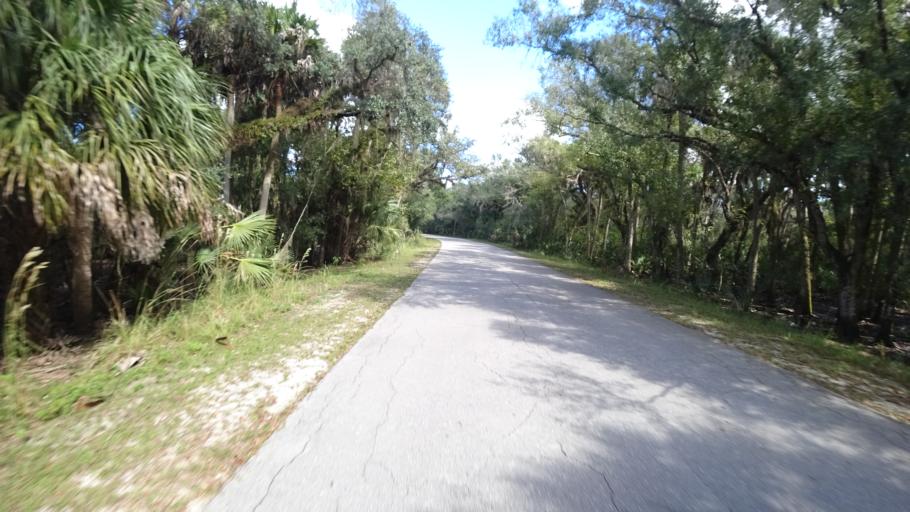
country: US
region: Florida
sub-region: Sarasota County
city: Lake Sarasota
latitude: 27.2845
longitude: -82.2574
